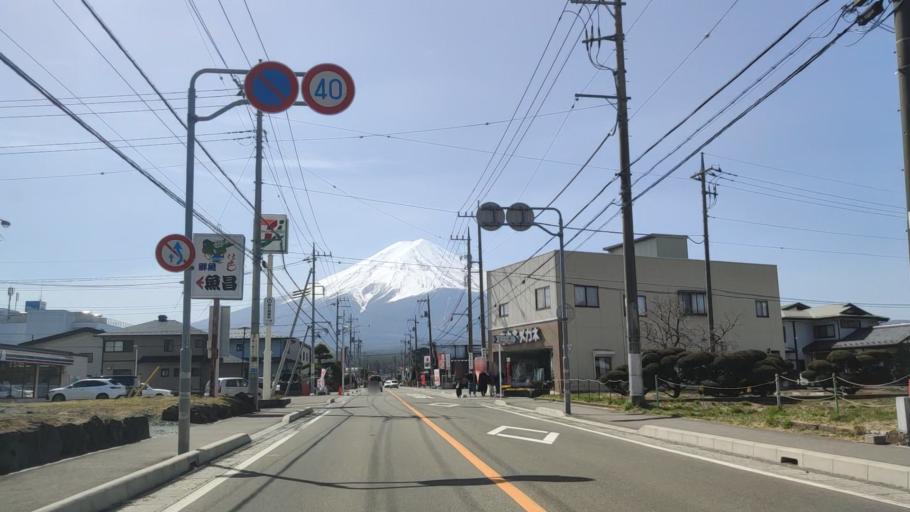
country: JP
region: Yamanashi
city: Fujikawaguchiko
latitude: 35.4922
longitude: 138.7636
